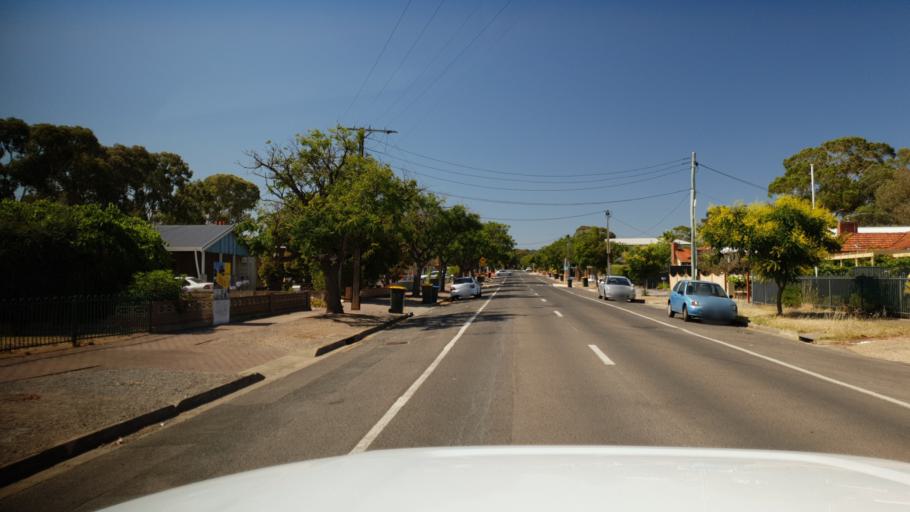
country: AU
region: South Australia
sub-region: Marion
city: Clovelly Park
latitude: -34.9971
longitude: 138.5789
